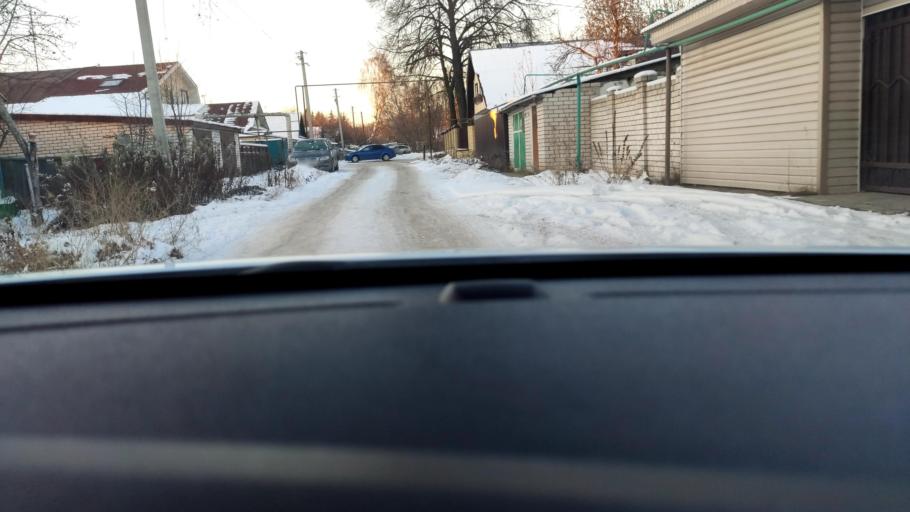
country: RU
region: Tatarstan
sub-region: Gorod Kazan'
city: Kazan
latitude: 55.8064
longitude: 49.0811
